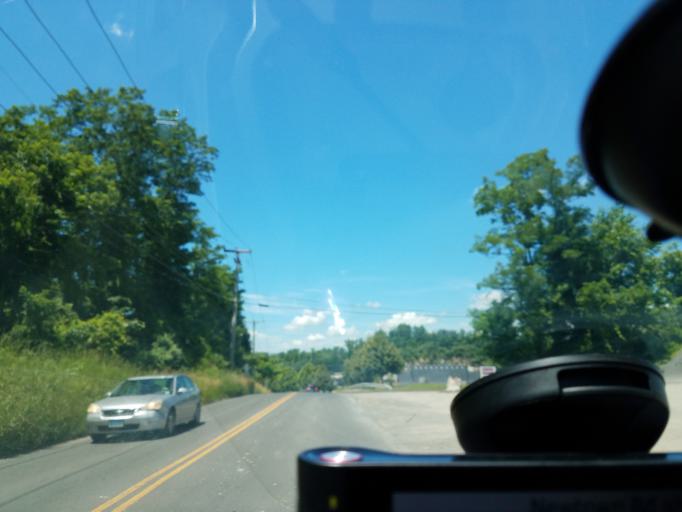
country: US
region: Connecticut
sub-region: Fairfield County
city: Bethel
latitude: 41.4041
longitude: -73.4163
